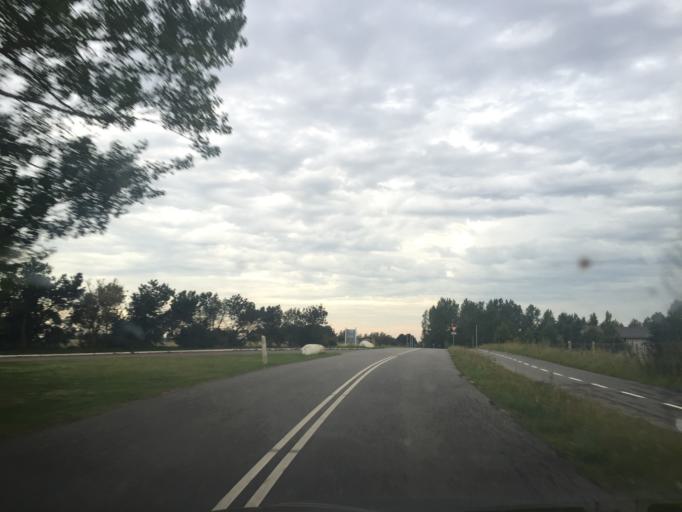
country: DK
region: Zealand
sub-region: Roskilde Kommune
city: Jyllinge
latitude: 55.7540
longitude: 12.1330
